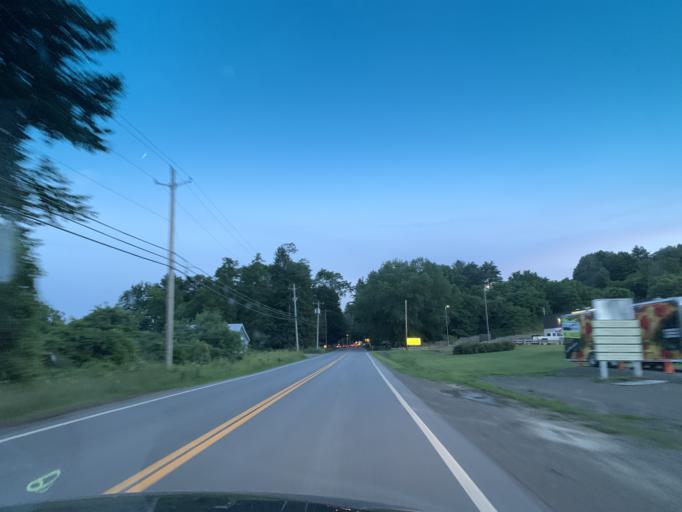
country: US
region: New York
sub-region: Chenango County
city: New Berlin
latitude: 42.6355
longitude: -75.3319
